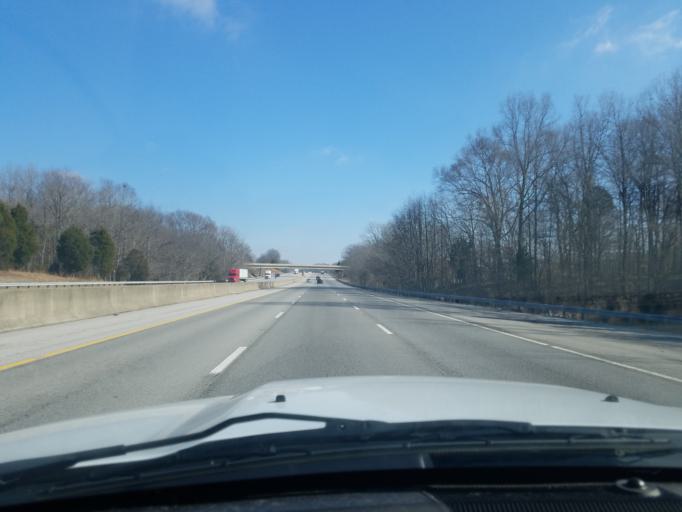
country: US
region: Kentucky
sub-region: Barren County
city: Cave City
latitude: 37.0619
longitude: -86.1049
